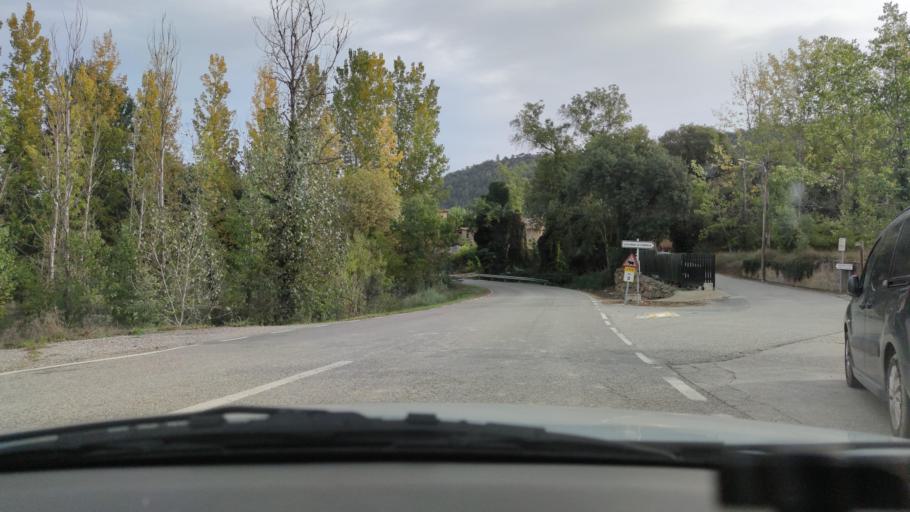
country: ES
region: Catalonia
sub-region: Provincia de Lleida
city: Artesa de Segre
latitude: 41.9083
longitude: 1.0700
